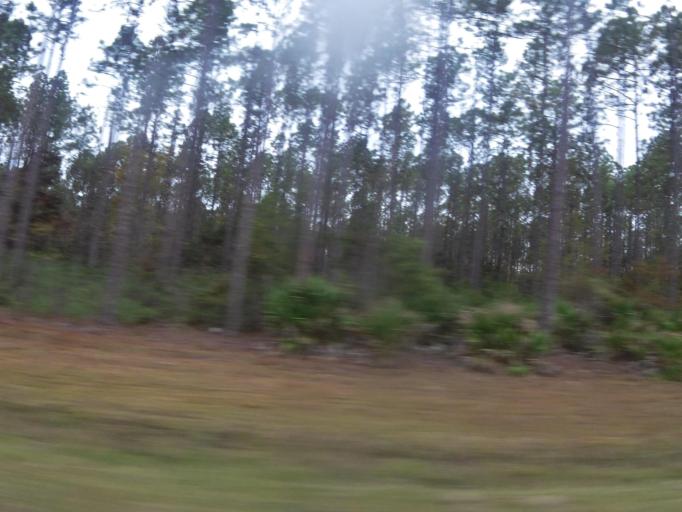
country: US
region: Georgia
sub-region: Charlton County
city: Folkston
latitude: 30.8911
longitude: -82.0633
